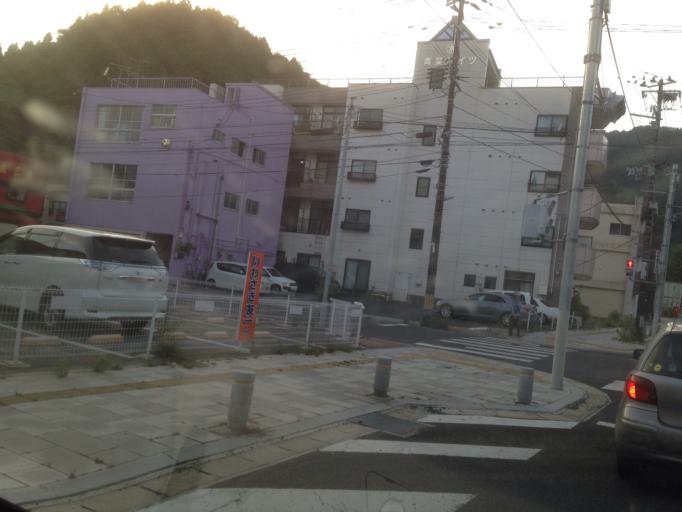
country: JP
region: Iwate
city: Kamaishi
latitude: 39.2742
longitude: 141.8814
